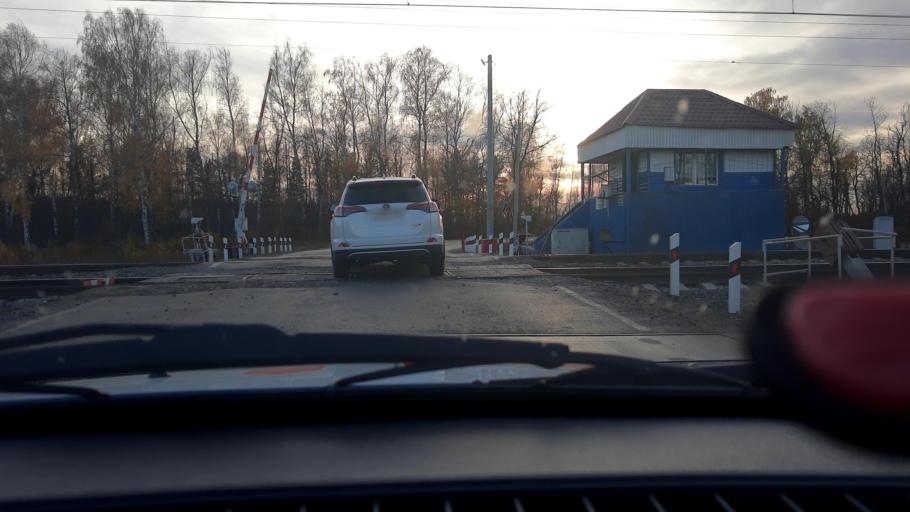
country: RU
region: Bashkortostan
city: Aksakovo
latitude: 54.0087
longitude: 54.3718
